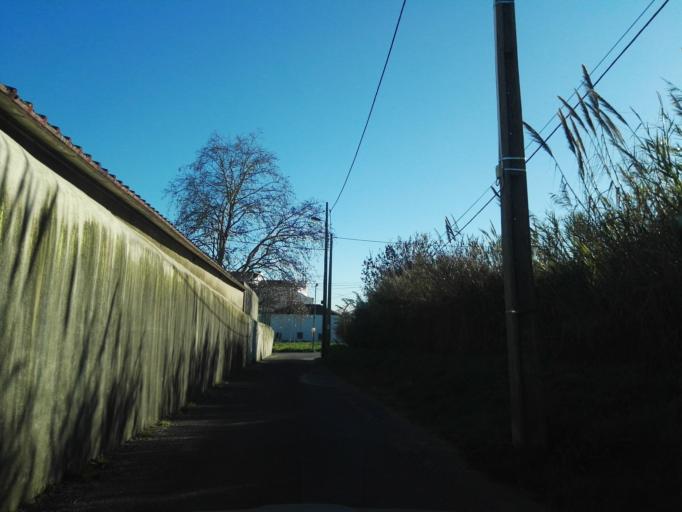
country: PT
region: Lisbon
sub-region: Odivelas
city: Pontinha
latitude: 38.7620
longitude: -9.1854
